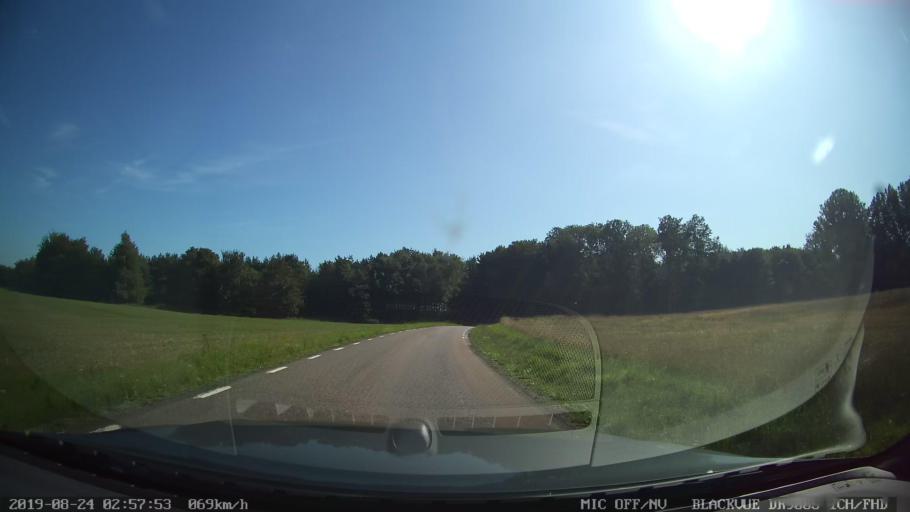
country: SE
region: Skane
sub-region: Skurups Kommun
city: Skurup
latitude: 55.4798
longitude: 13.4120
